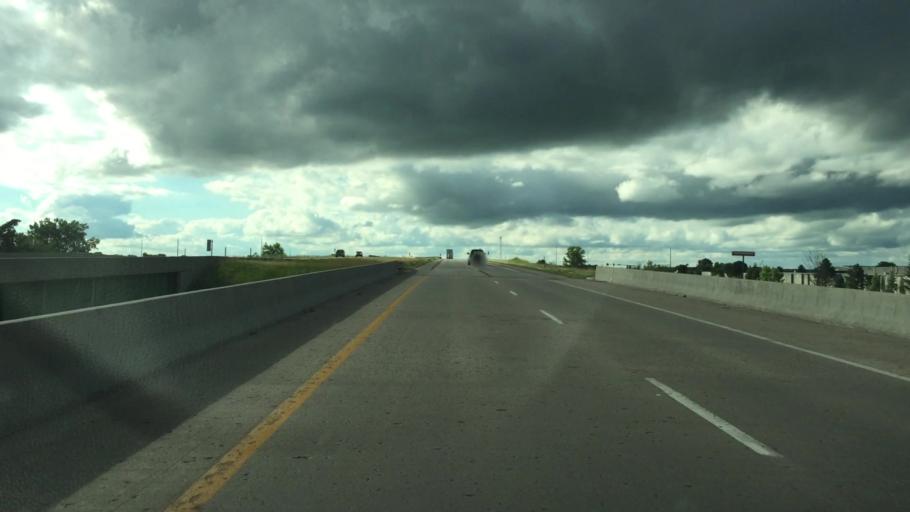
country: US
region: Iowa
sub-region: Polk County
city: Altoona
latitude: 41.6442
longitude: -93.5103
